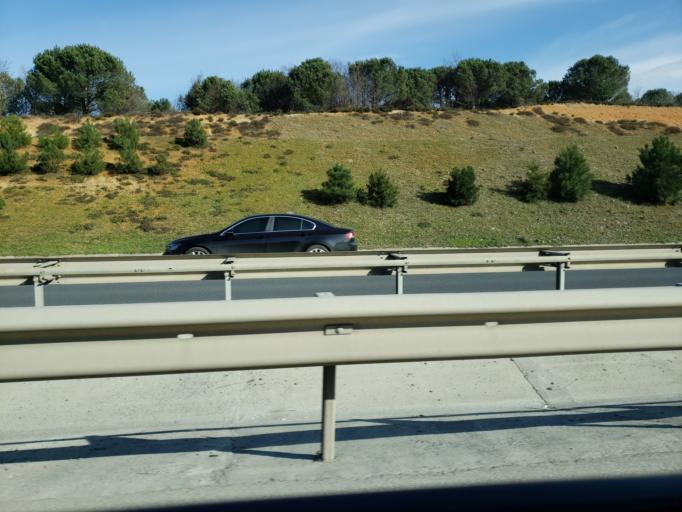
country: TR
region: Istanbul
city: Kemerburgaz
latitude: 41.1470
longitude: 28.9020
